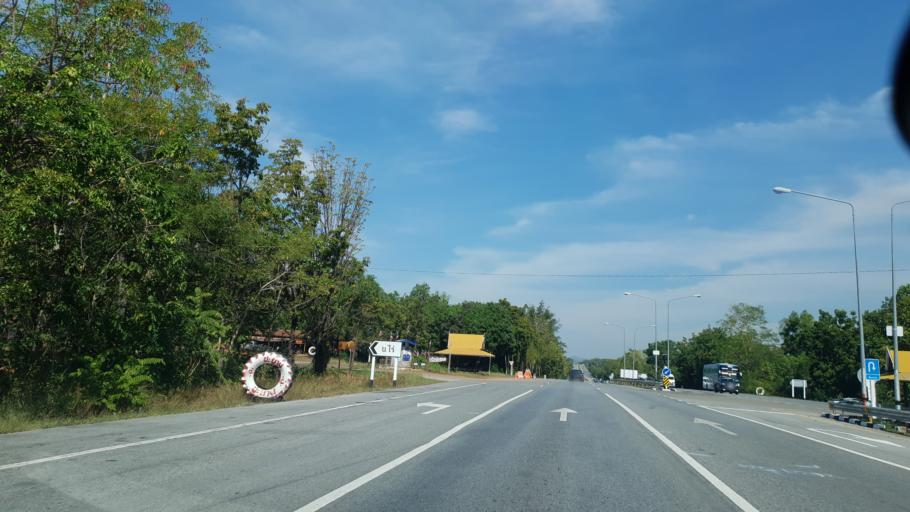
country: TH
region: Uttaradit
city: Thong Saen Khan
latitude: 17.4330
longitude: 100.2283
